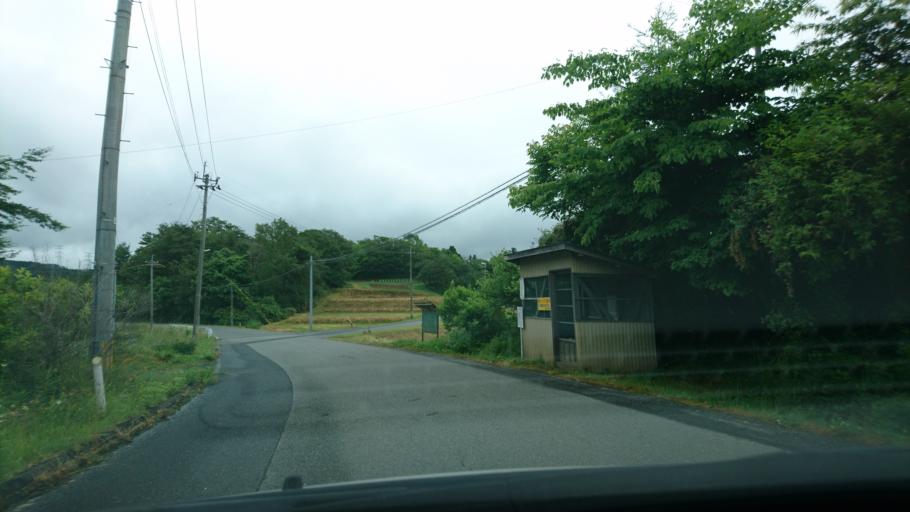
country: JP
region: Iwate
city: Ichinoseki
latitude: 38.9124
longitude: 141.2018
